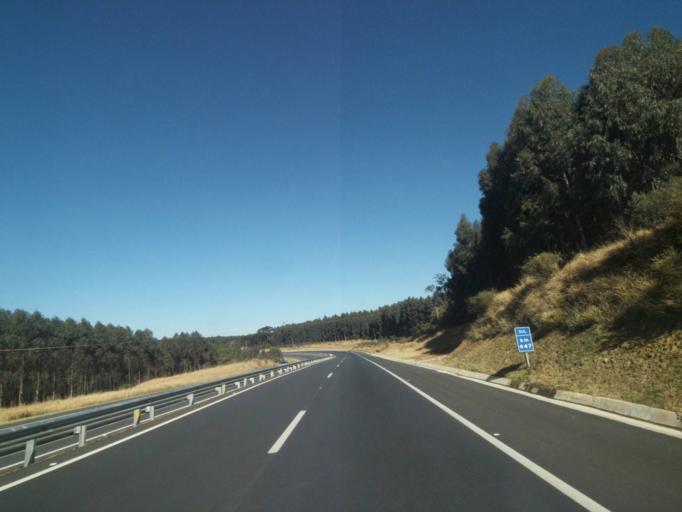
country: BR
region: Parana
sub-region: Tibagi
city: Tibagi
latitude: -24.8535
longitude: -50.4611
